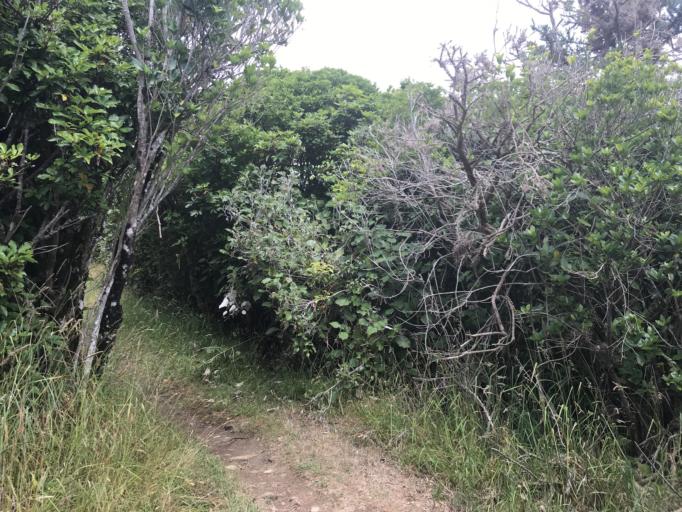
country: NZ
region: Marlborough
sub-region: Marlborough District
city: Picton
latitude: -41.2112
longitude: 174.0135
